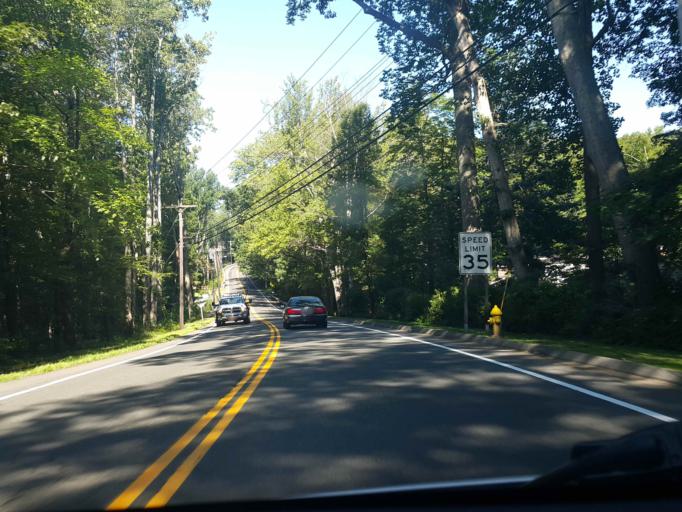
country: US
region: Connecticut
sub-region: New Haven County
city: North Branford
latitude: 41.3190
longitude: -72.7536
